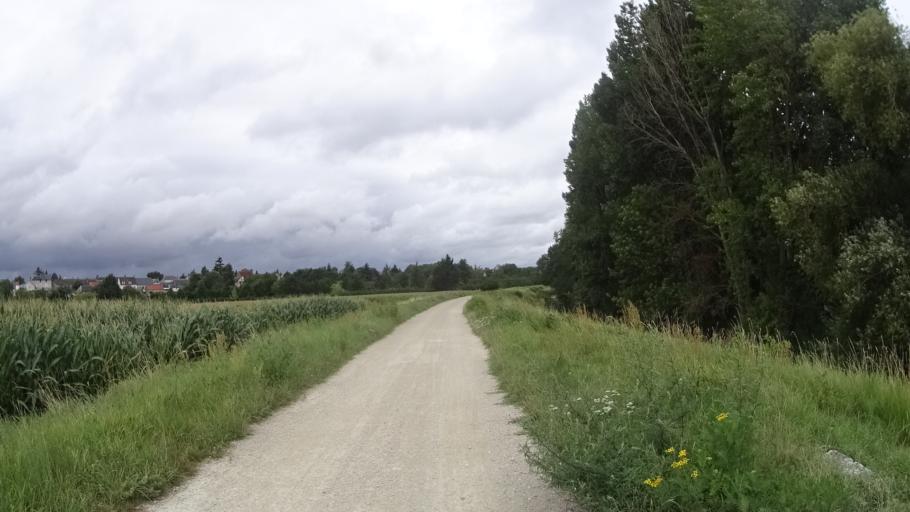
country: FR
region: Centre
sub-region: Departement du Loiret
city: Baule
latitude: 47.8100
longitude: 1.6834
